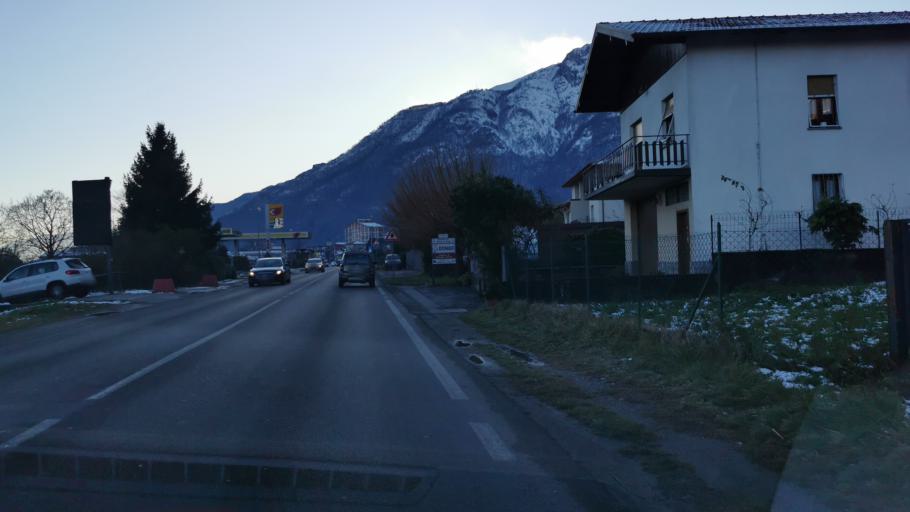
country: IT
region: Lombardy
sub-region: Provincia di Como
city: Consiglio di Rumo
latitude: 46.1371
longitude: 9.2889
